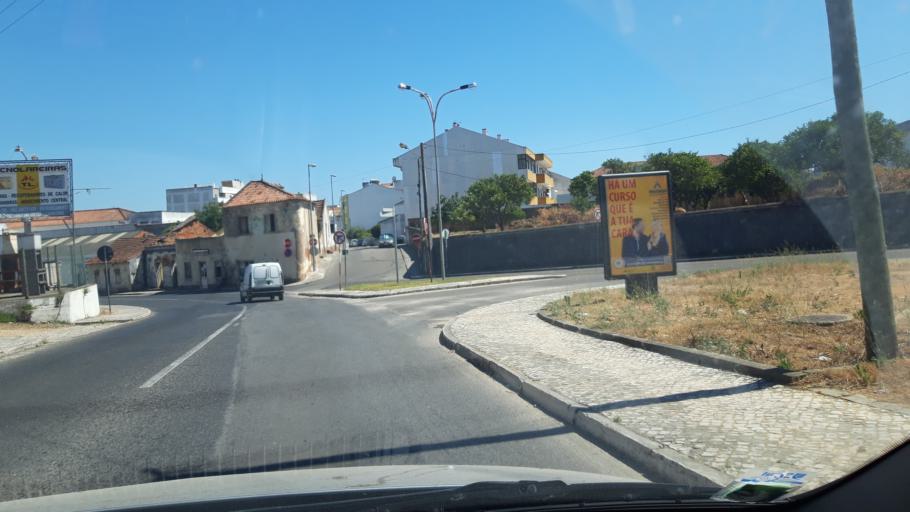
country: PT
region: Santarem
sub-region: Entroncamento
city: Entroncamento
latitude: 39.4639
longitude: -8.4637
